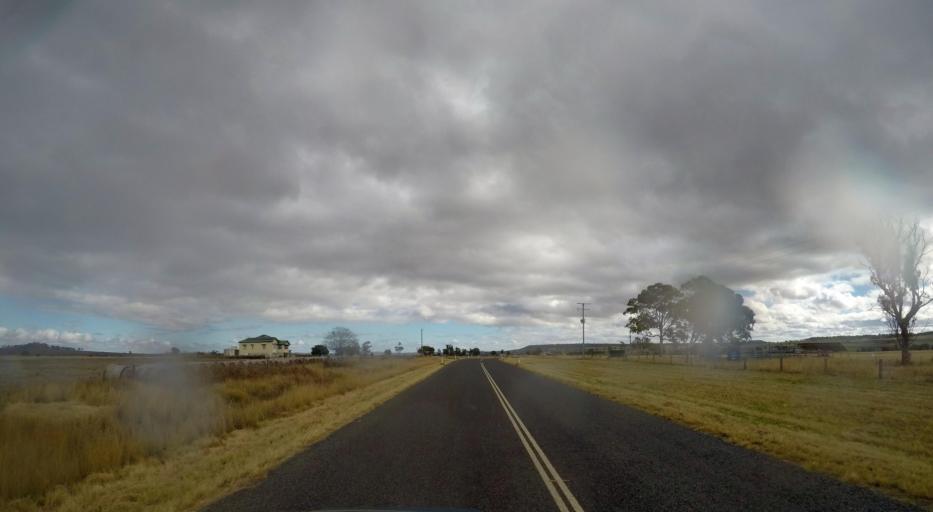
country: AU
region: Queensland
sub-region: Southern Downs
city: Warwick
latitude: -28.0457
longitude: 152.0523
